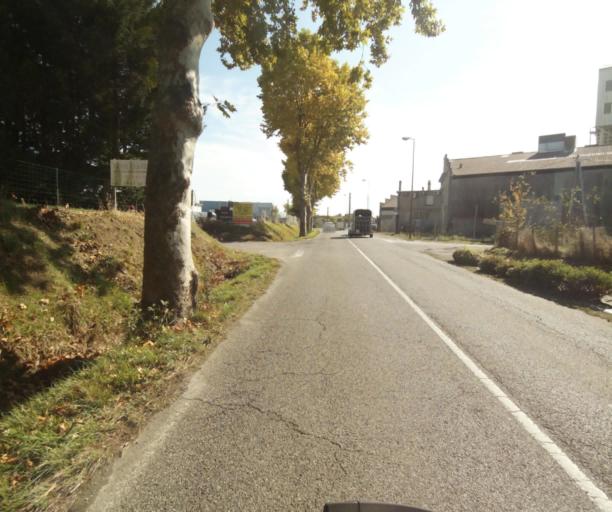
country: FR
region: Midi-Pyrenees
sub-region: Departement du Tarn-et-Garonne
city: Verdun-sur-Garonne
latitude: 43.8547
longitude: 1.2240
